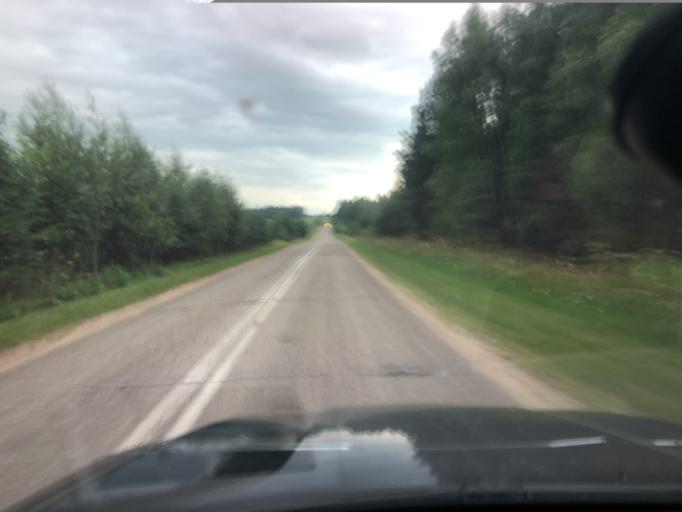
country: RU
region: Jaroslavl
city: Pereslavl'-Zalesskiy
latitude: 57.0207
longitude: 38.9477
